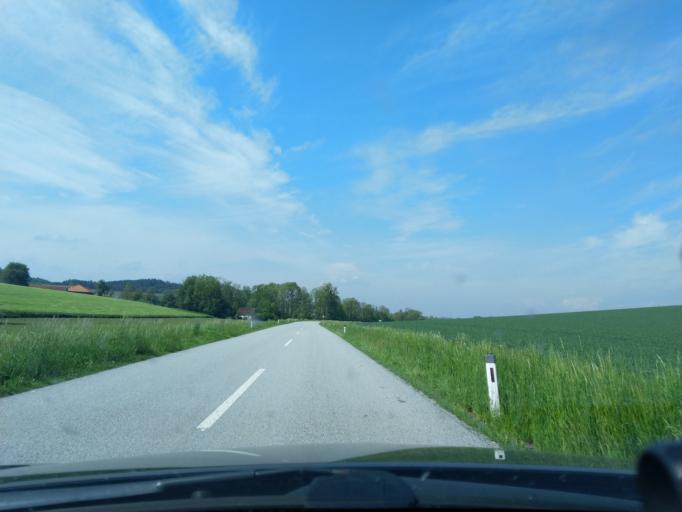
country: DE
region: Bavaria
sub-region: Lower Bavaria
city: Bad Fussing
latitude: 48.3013
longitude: 13.3771
